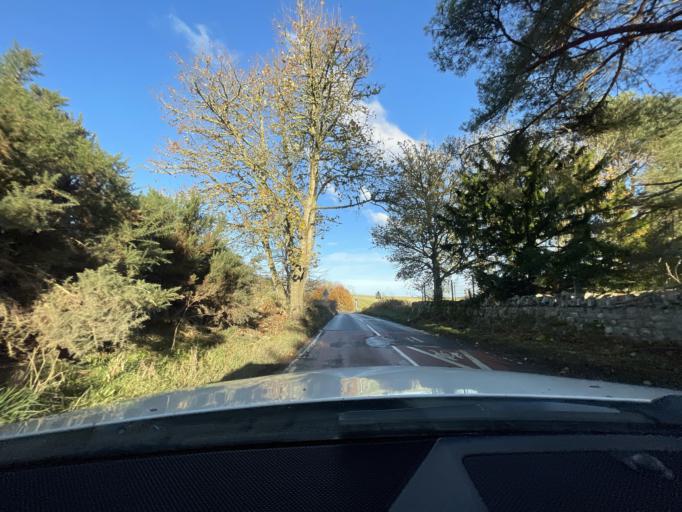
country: GB
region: Scotland
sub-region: Highland
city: Inverness
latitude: 57.3965
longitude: -4.3199
